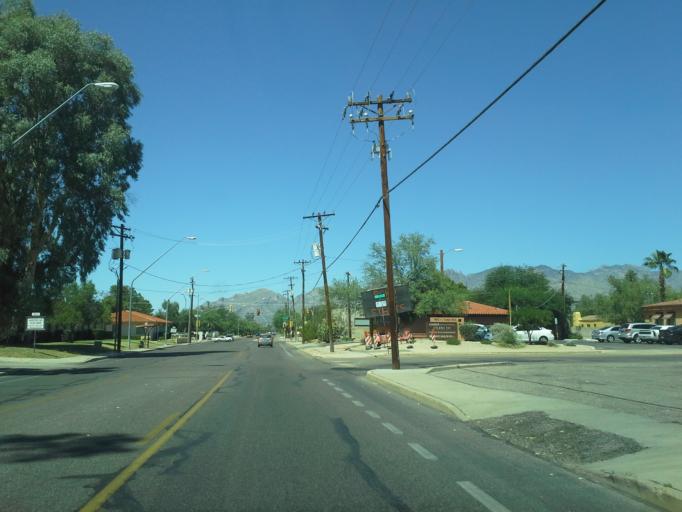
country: US
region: Arizona
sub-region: Pima County
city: Tucson
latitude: 32.2414
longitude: -110.9353
